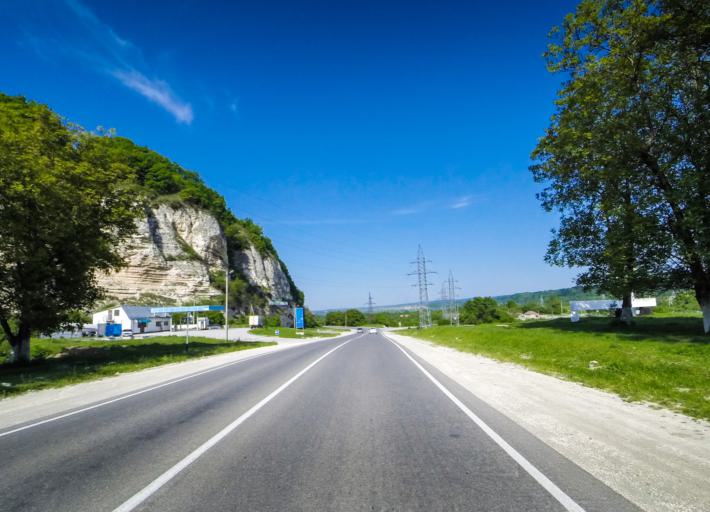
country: RU
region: Kabardino-Balkariya
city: Kashkhatau
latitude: 43.3303
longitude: 43.6426
